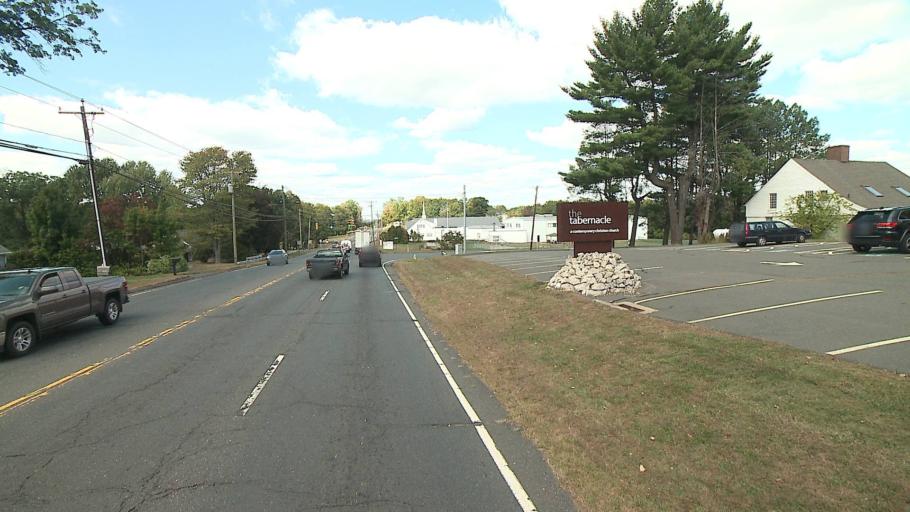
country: US
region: Connecticut
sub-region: Hartford County
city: Plainville
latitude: 41.6277
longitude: -72.8999
